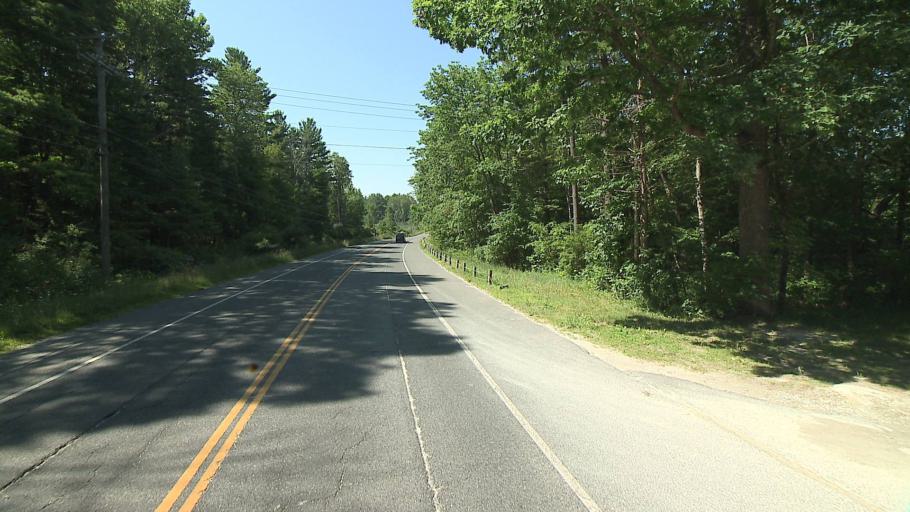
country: US
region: Connecticut
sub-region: Litchfield County
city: Canaan
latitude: 41.9365
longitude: -73.4406
